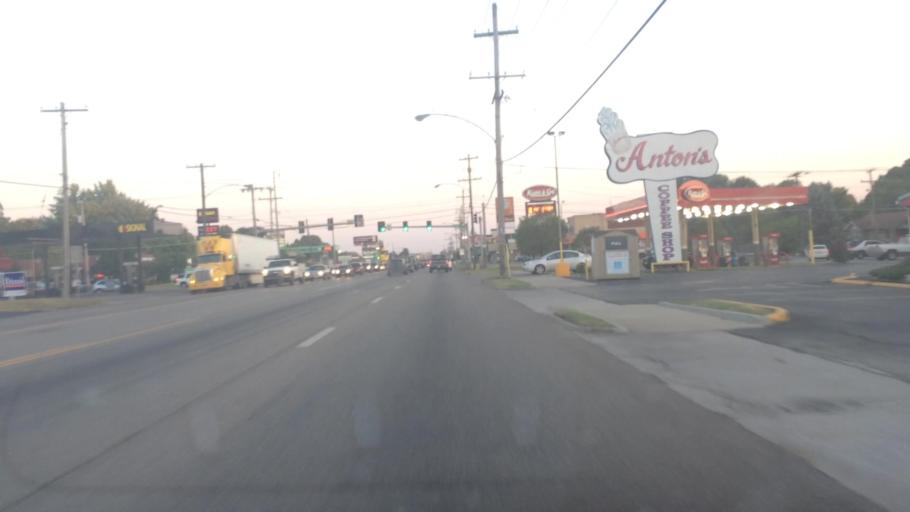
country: US
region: Missouri
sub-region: Greene County
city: Springfield
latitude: 37.1972
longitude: -93.2621
